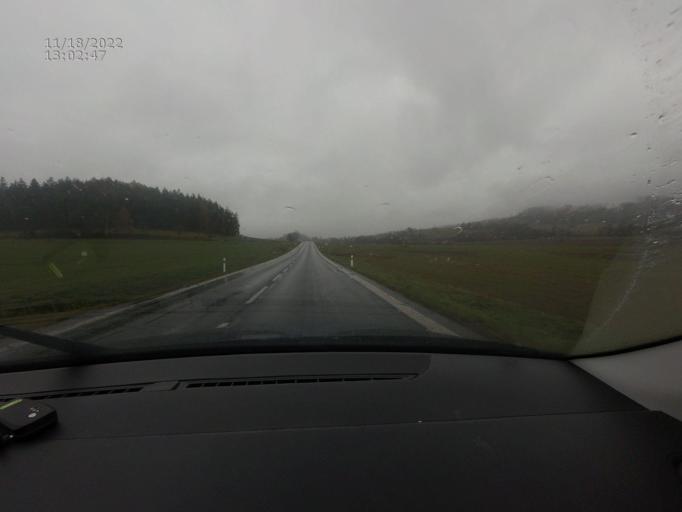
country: CZ
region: Plzensky
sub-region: Okres Klatovy
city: Kolinec
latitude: 49.3474
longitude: 13.4439
